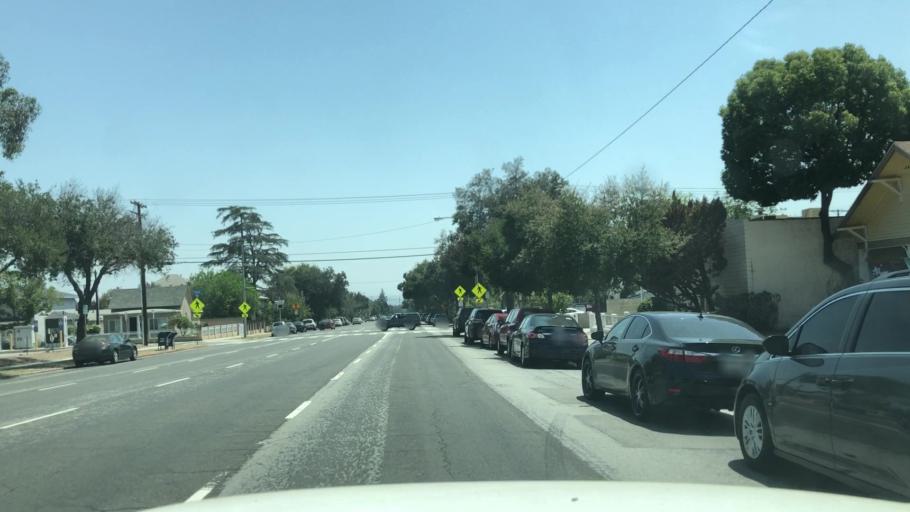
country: US
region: California
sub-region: Los Angeles County
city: Azusa
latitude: 34.1324
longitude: -117.9089
